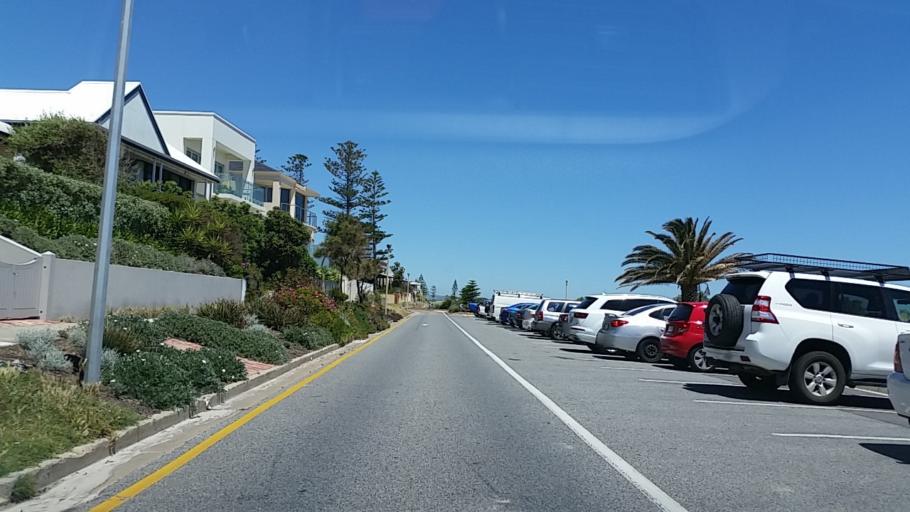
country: AU
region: South Australia
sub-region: Charles Sturt
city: Grange
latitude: -34.9042
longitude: 138.4897
